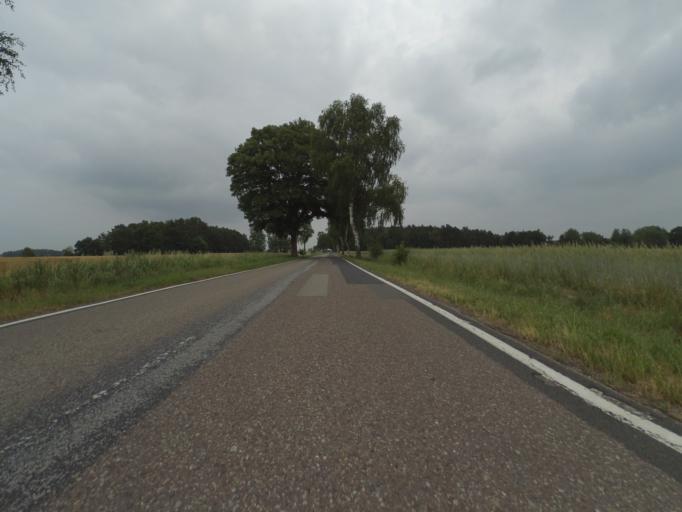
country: DE
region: Mecklenburg-Vorpommern
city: Siggelkow
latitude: 53.3764
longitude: 11.9878
